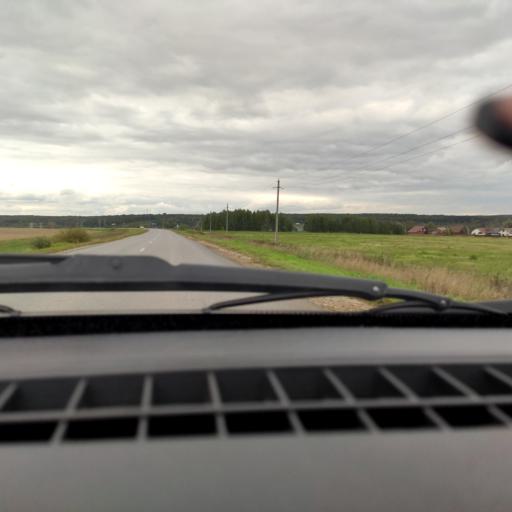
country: RU
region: Bashkortostan
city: Iglino
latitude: 54.7498
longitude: 56.3998
